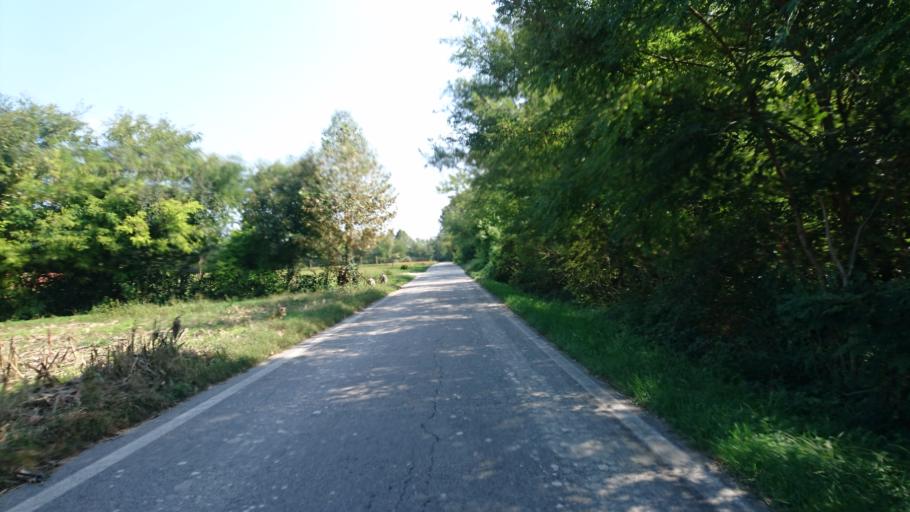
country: IT
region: Veneto
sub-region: Provincia di Padova
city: San Giorgio in Bosco
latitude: 45.5708
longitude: 11.7853
